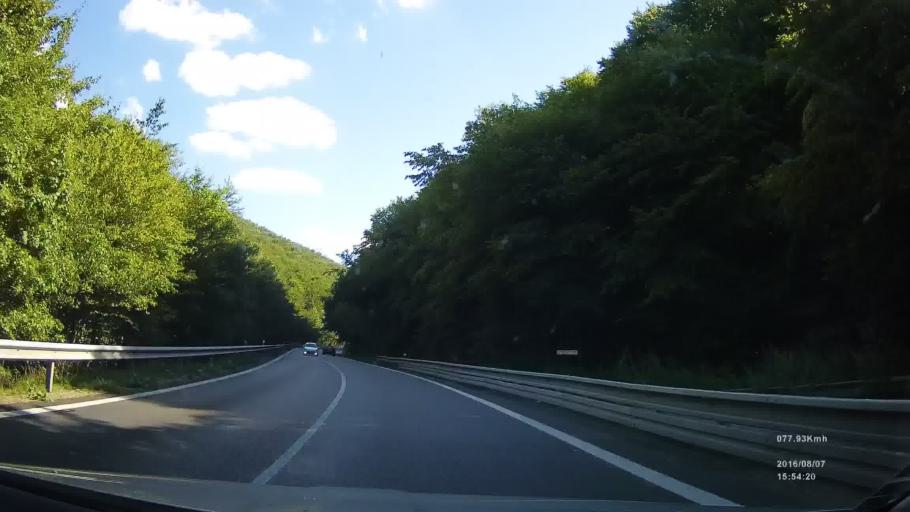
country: SK
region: Presovsky
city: Giraltovce
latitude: 49.0887
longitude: 21.4439
